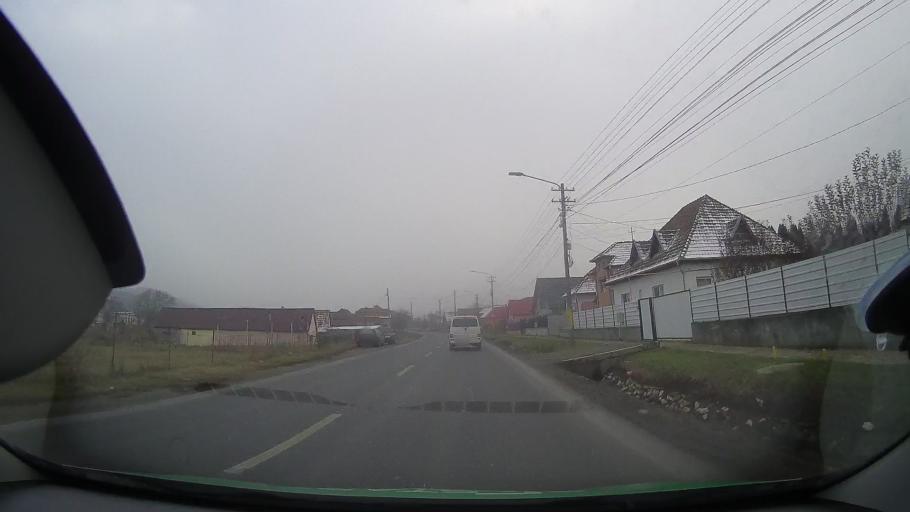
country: RO
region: Mures
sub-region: Municipiul Tarnaveni
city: Tarnaveni
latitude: 46.3131
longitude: 24.2975
